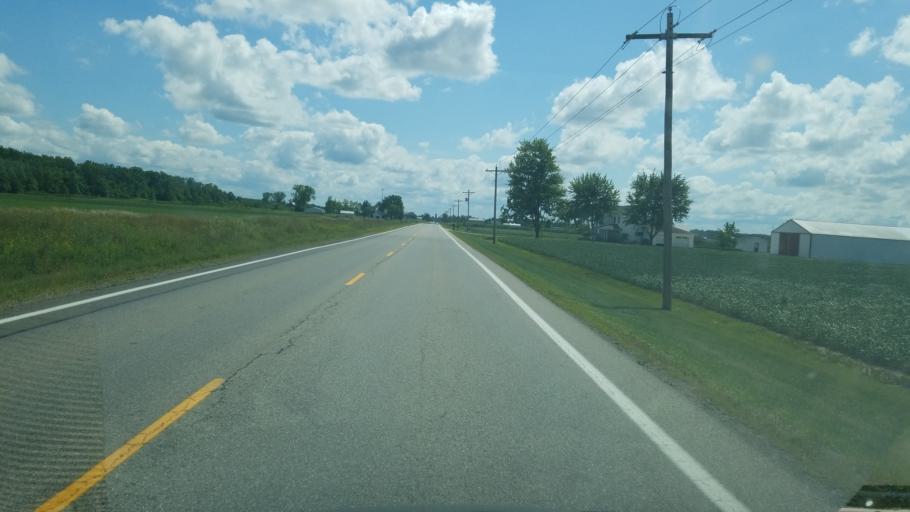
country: US
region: Ohio
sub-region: Putnam County
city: Kalida
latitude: 41.0199
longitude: -84.1980
